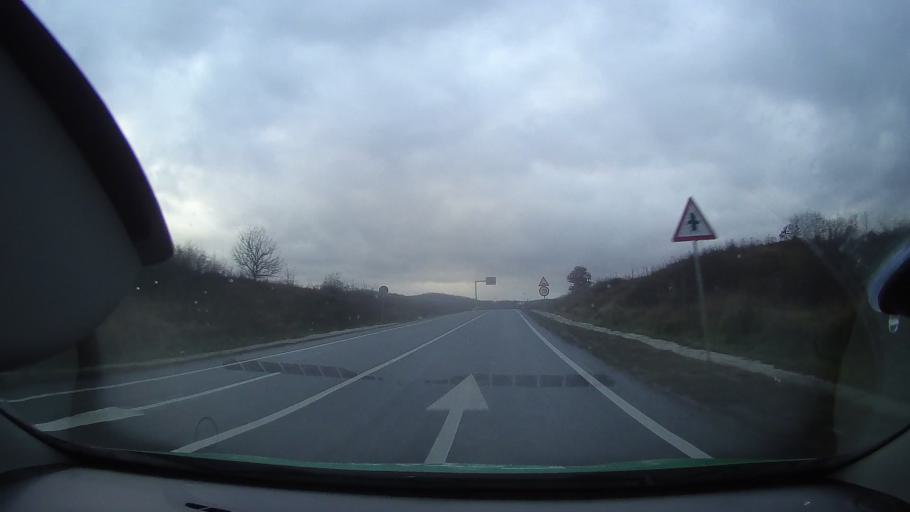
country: RO
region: Hunedoara
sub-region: Comuna Baia de Cris
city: Baia de Cris
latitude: 46.1702
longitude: 22.7210
